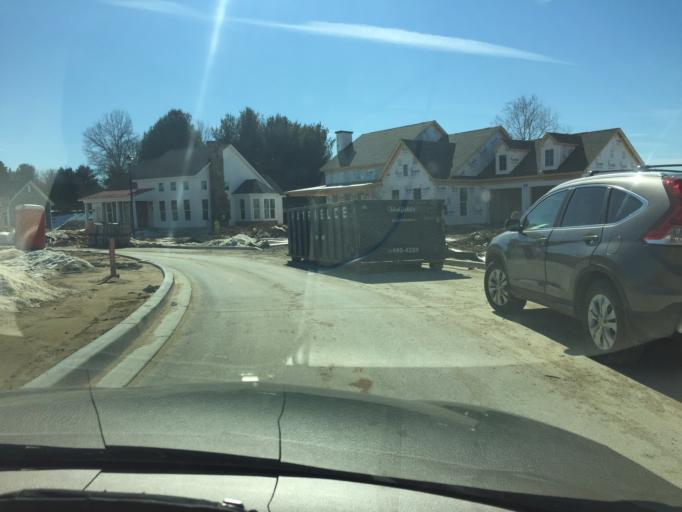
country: US
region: Maryland
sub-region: Howard County
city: Columbia
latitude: 39.2706
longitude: -76.8443
